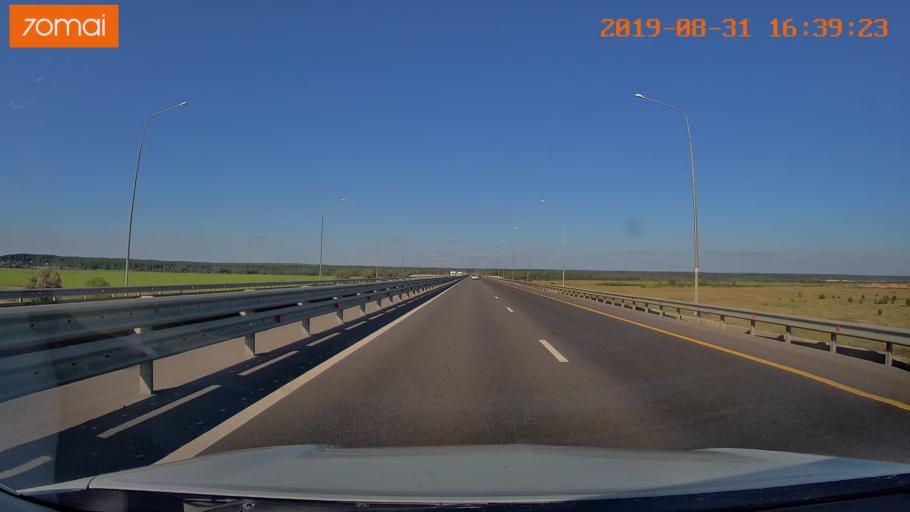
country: RU
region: Kaluga
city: Kurovskoye
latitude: 54.5507
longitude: 36.0248
